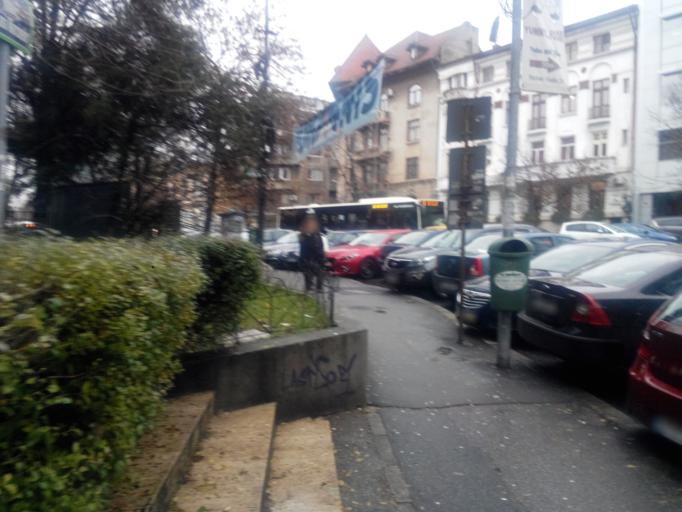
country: RO
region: Bucuresti
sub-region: Municipiul Bucuresti
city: Bucuresti
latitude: 44.4399
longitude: 26.0911
